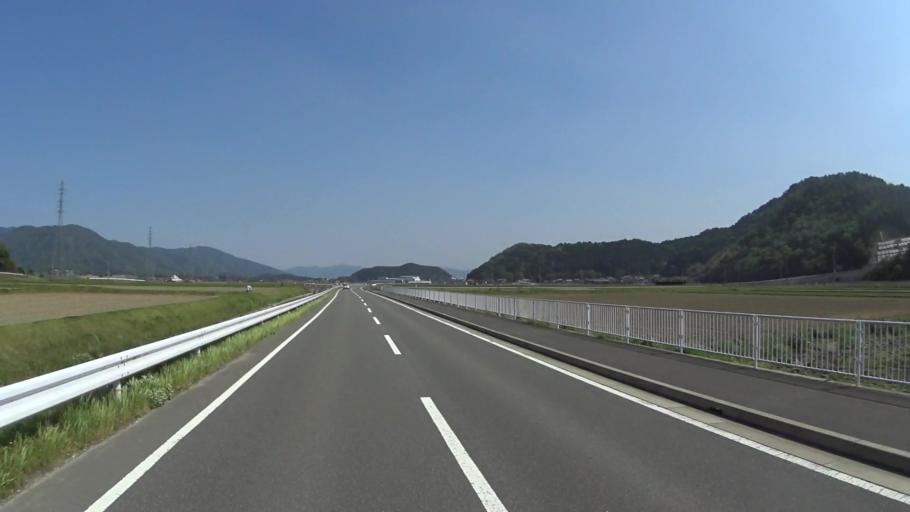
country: JP
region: Kyoto
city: Kameoka
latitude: 35.1002
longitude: 135.5304
